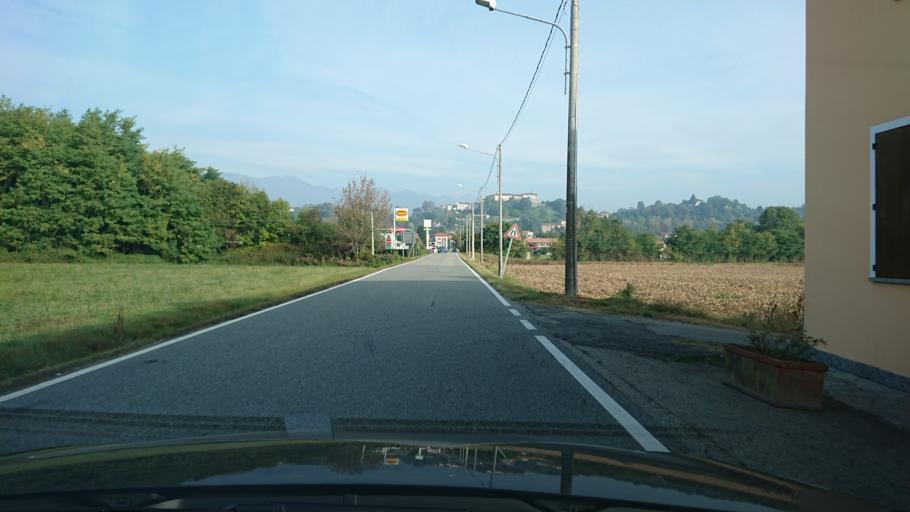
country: IT
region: Piedmont
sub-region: Provincia di Biella
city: Valdengo
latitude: 45.5654
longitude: 8.1316
